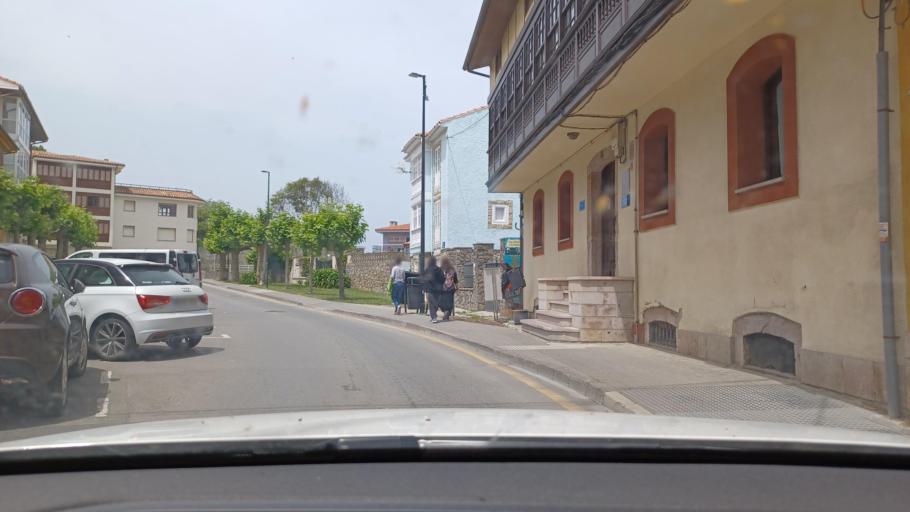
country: ES
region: Asturias
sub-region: Province of Asturias
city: Llanes
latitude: 43.4217
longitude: -4.7512
